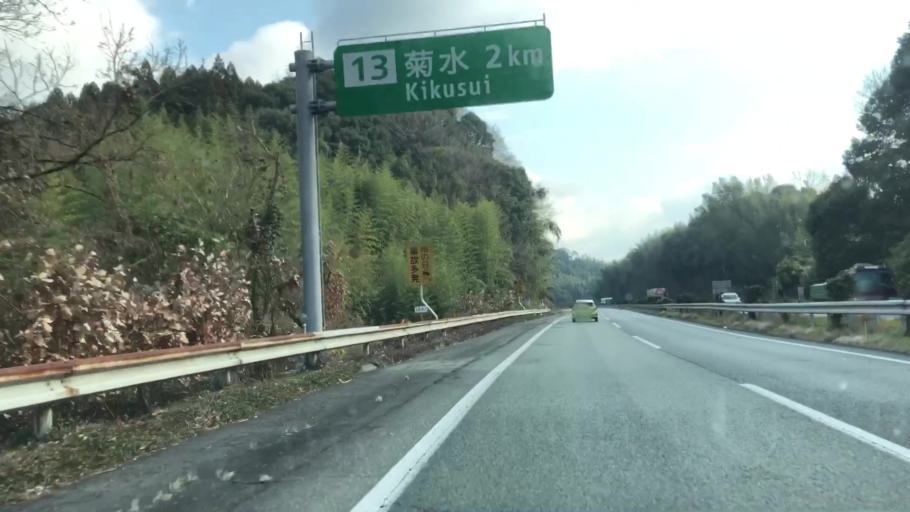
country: JP
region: Kumamoto
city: Tamana
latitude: 33.0001
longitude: 130.5905
